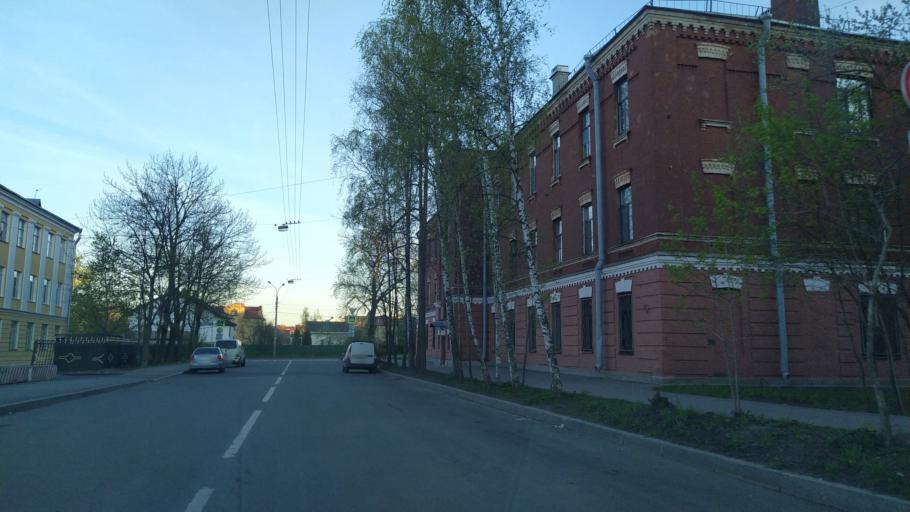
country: RU
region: St.-Petersburg
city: Pushkin
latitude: 59.7044
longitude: 30.4114
